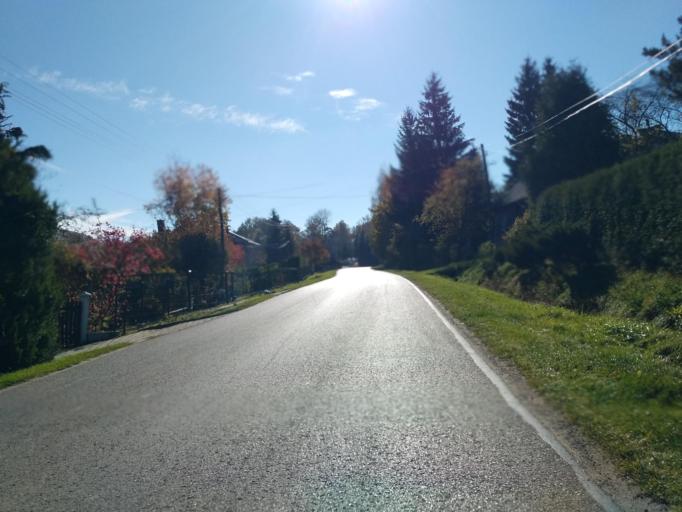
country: PL
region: Subcarpathian Voivodeship
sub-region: Powiat ropczycko-sedziszowski
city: Iwierzyce
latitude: 49.9876
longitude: 21.7264
